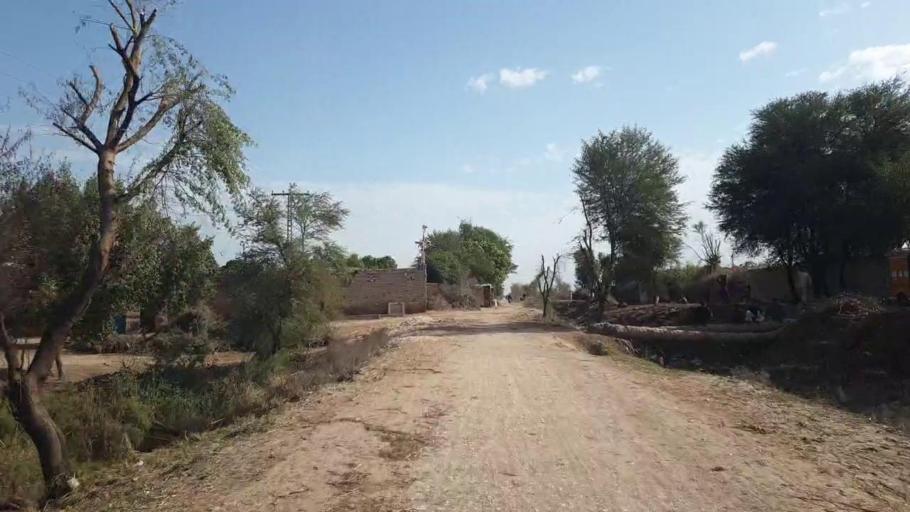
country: PK
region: Sindh
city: Shahdadpur
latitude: 26.0214
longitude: 68.4933
